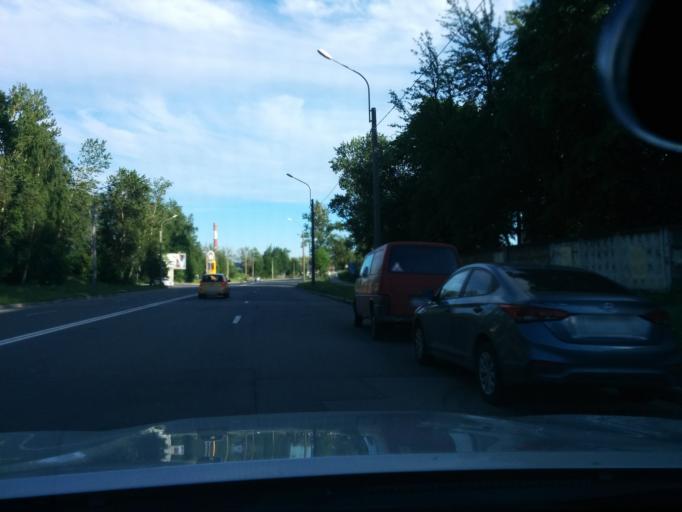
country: RU
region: St.-Petersburg
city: Kushelevka
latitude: 59.9811
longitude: 30.3653
